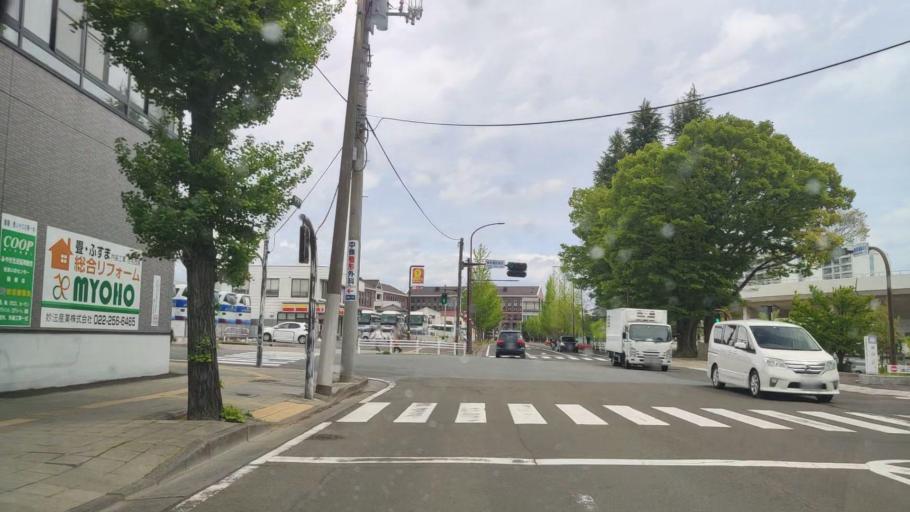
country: JP
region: Miyagi
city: Sendai-shi
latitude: 38.2582
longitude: 140.9018
